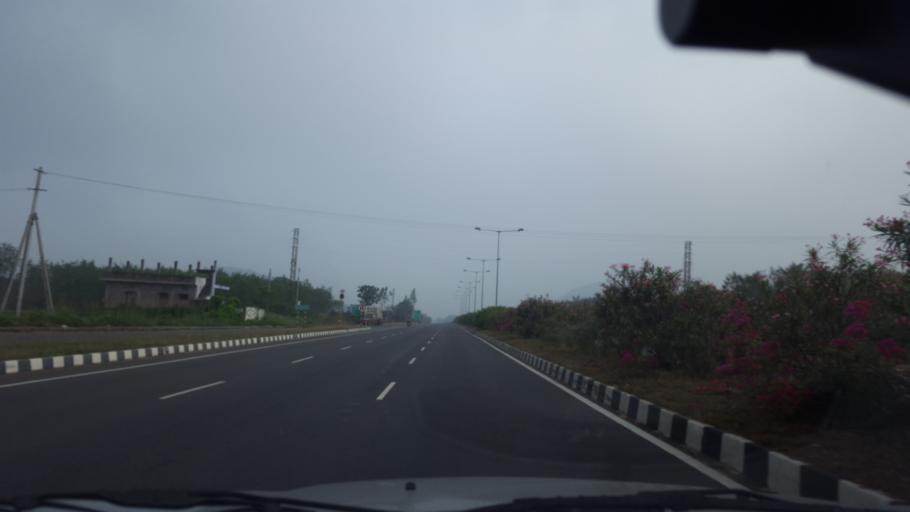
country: IN
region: Andhra Pradesh
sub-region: Prakasam
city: pedda nakkalapalem
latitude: 15.8703
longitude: 80.0642
